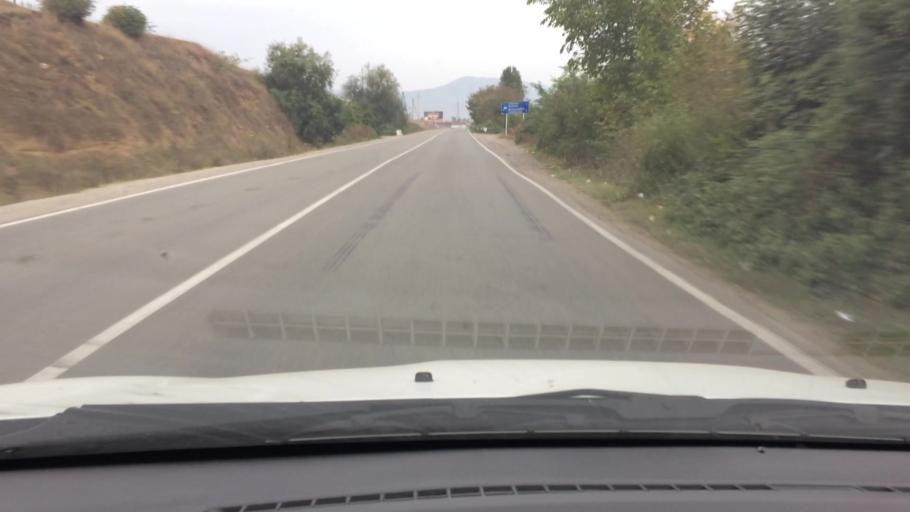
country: AM
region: Tavush
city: Bagratashen
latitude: 41.2288
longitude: 44.8247
